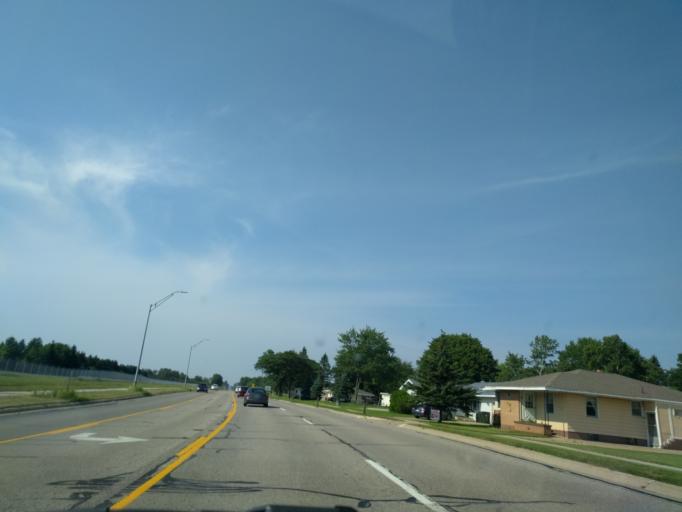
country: US
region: Michigan
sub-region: Delta County
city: Escanaba
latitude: 45.7177
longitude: -87.0802
